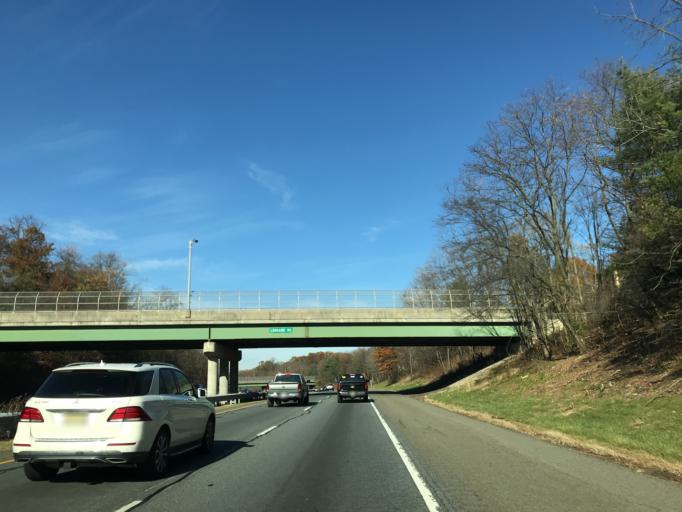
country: US
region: New Jersey
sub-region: Morris County
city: Madison
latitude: 40.7686
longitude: -74.4032
